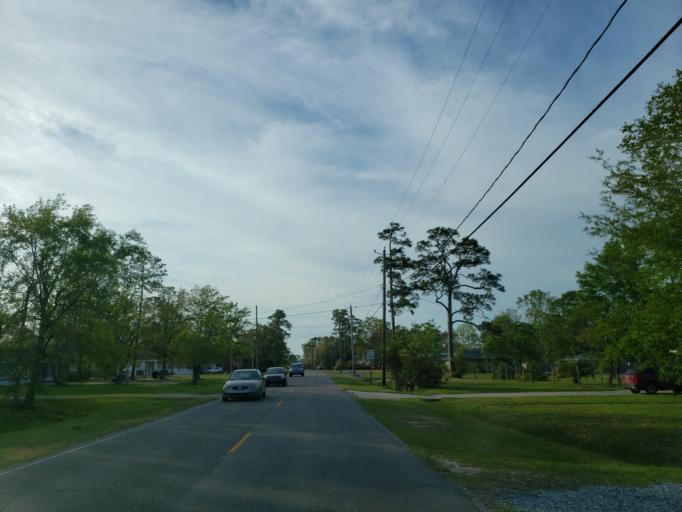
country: US
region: Mississippi
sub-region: Harrison County
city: West Gulfport
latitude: 30.4121
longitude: -89.0545
